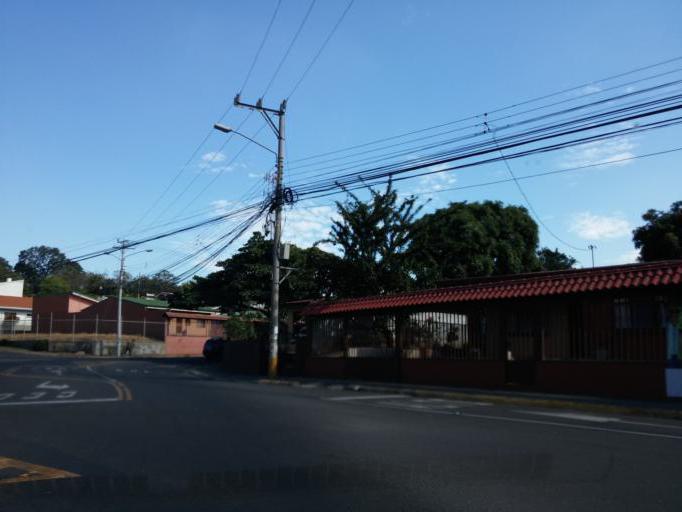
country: CR
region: Heredia
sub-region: Canton de Belen
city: San Antonio
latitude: 9.9837
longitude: -84.1913
